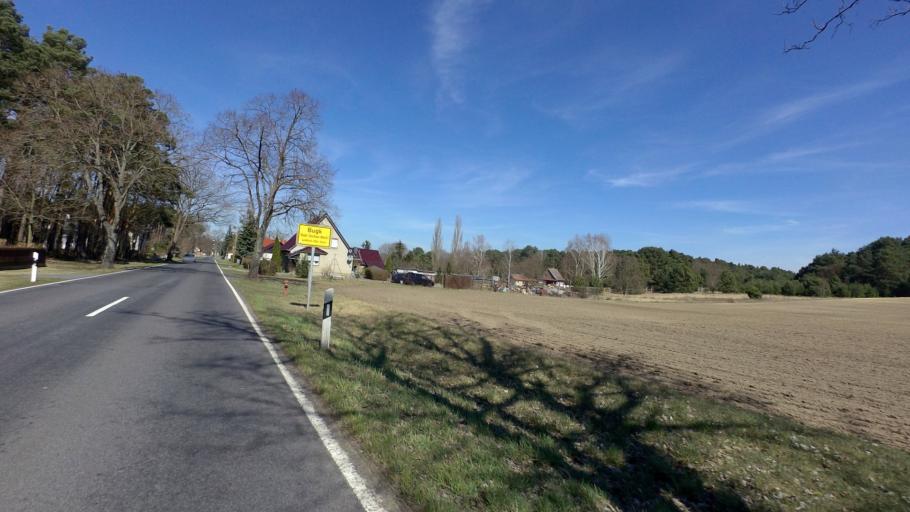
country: DE
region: Brandenburg
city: Storkow
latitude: 52.1902
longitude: 13.9184
